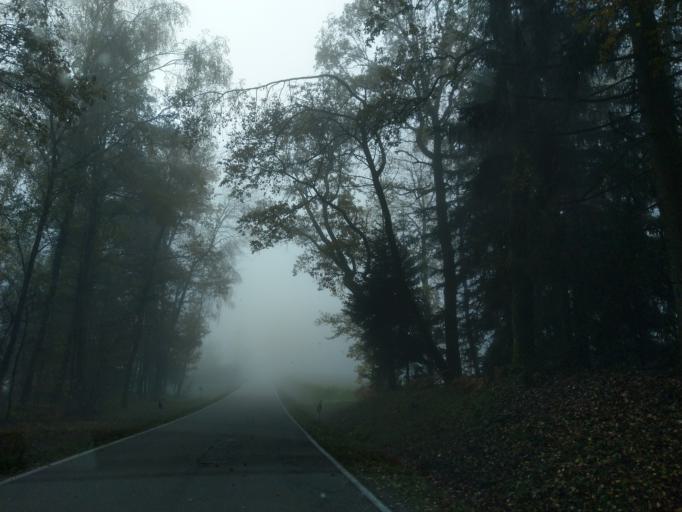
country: DE
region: Bavaria
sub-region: Lower Bavaria
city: Iggensbach
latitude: 48.7670
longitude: 13.1419
